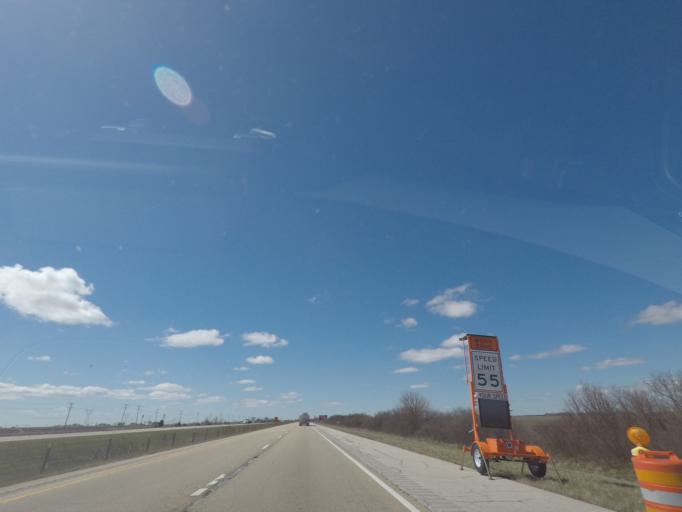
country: US
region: Illinois
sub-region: Livingston County
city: Dwight
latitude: 41.1301
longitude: -88.3822
